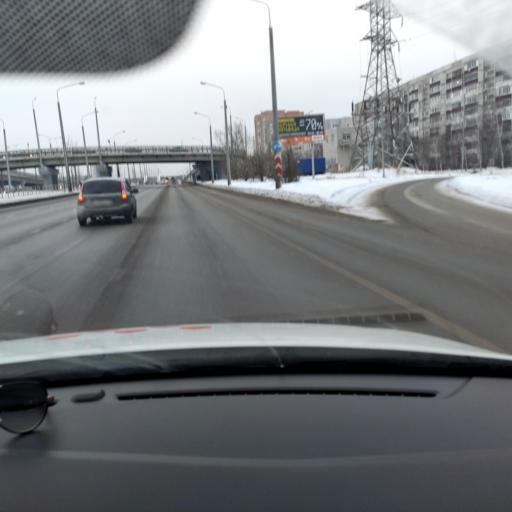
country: RU
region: Tatarstan
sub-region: Gorod Kazan'
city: Kazan
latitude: 55.7754
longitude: 49.2256
